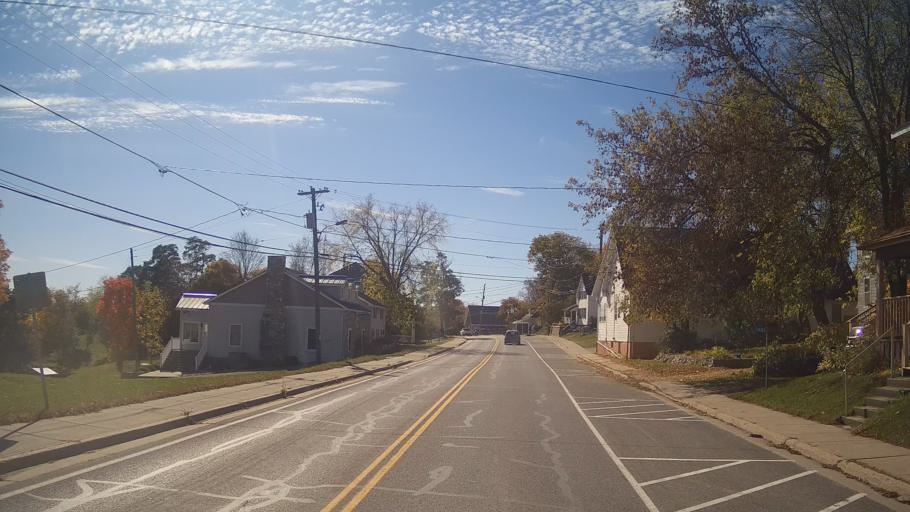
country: CA
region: Ontario
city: Perth
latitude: 44.7713
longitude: -76.6877
